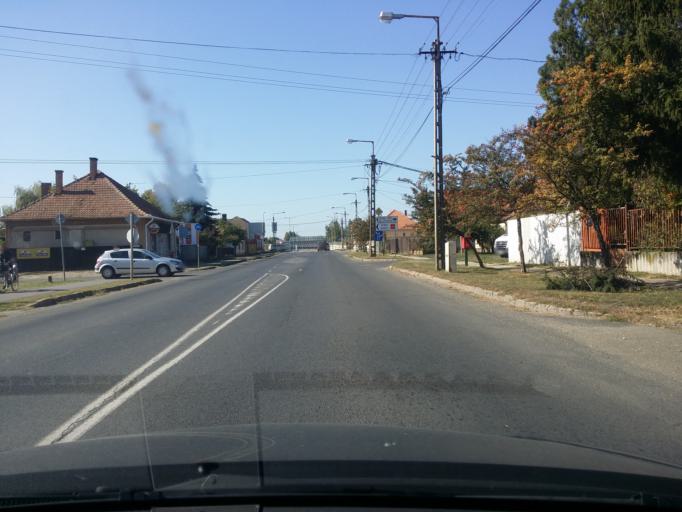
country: HU
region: Bekes
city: Gyomaendrod
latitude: 46.9351
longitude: 20.8195
